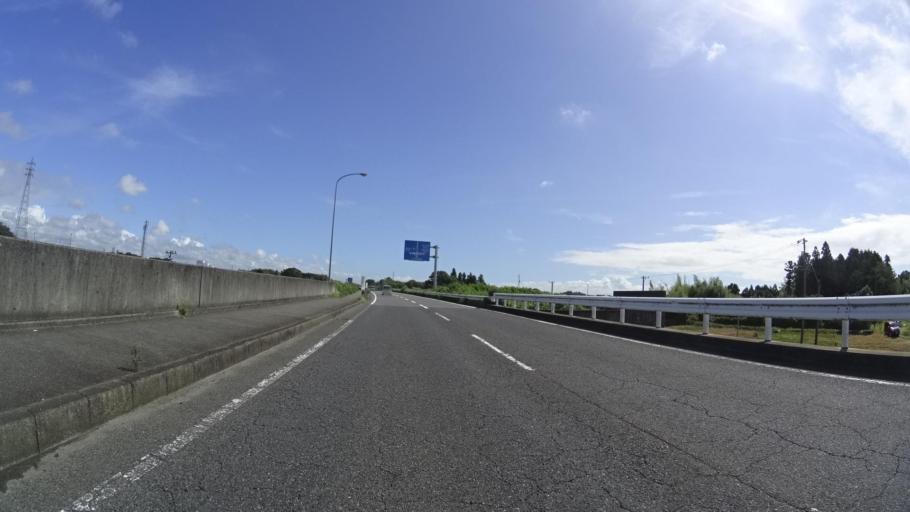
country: JP
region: Mie
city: Kawage
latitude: 34.8372
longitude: 136.5448
